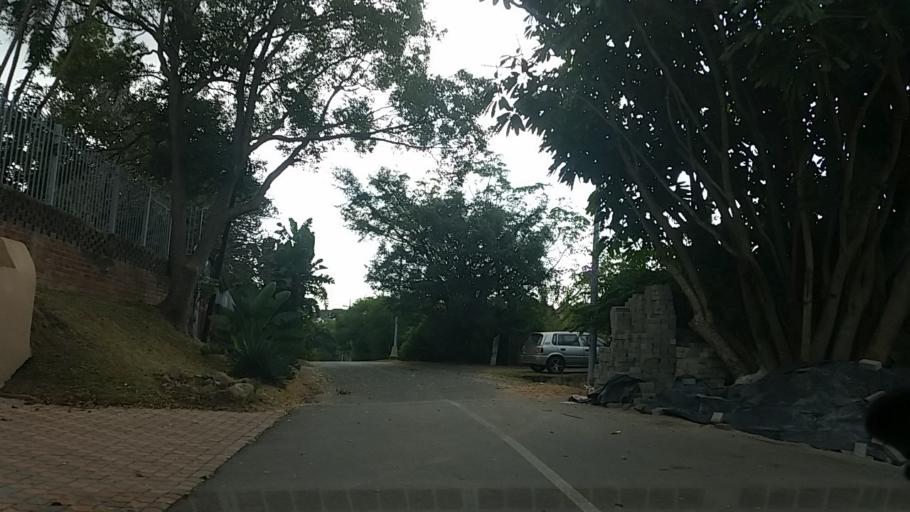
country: ZA
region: KwaZulu-Natal
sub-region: eThekwini Metropolitan Municipality
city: Berea
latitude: -29.8343
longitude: 30.9452
